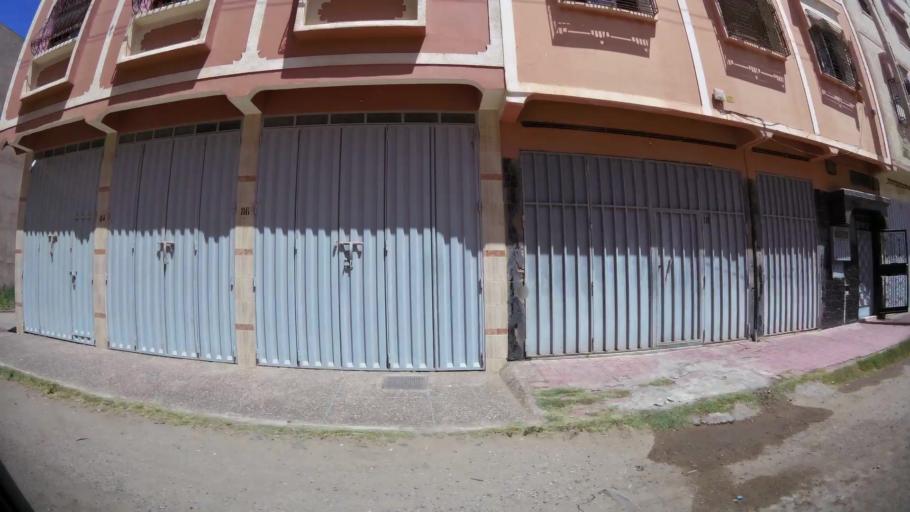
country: MA
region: Souss-Massa-Draa
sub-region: Inezgane-Ait Mellou
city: Inezgane
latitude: 30.3367
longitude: -9.4994
